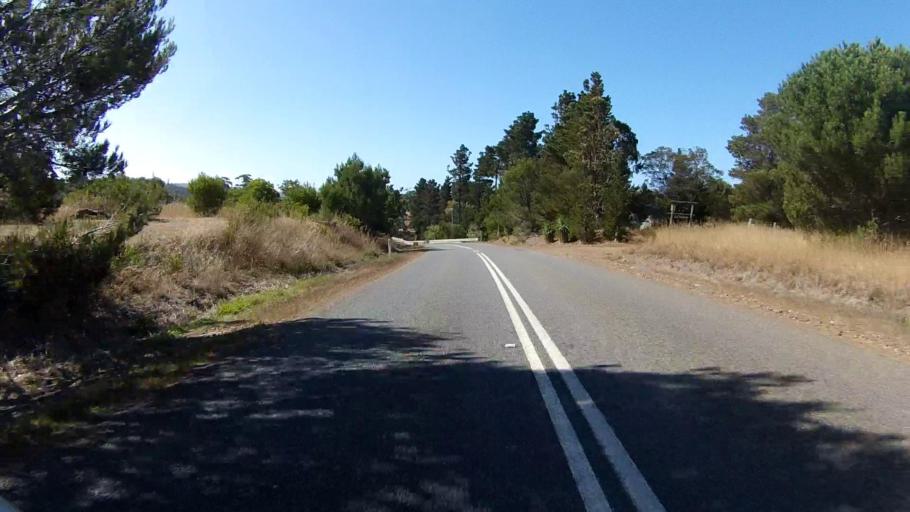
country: AU
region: Tasmania
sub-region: Sorell
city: Sorell
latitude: -42.2871
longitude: 147.9963
